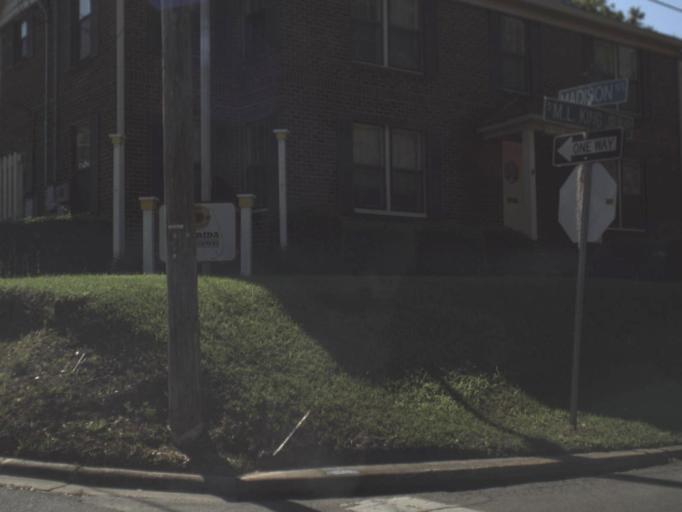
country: US
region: Florida
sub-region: Leon County
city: Tallahassee
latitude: 30.4366
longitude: -84.2857
